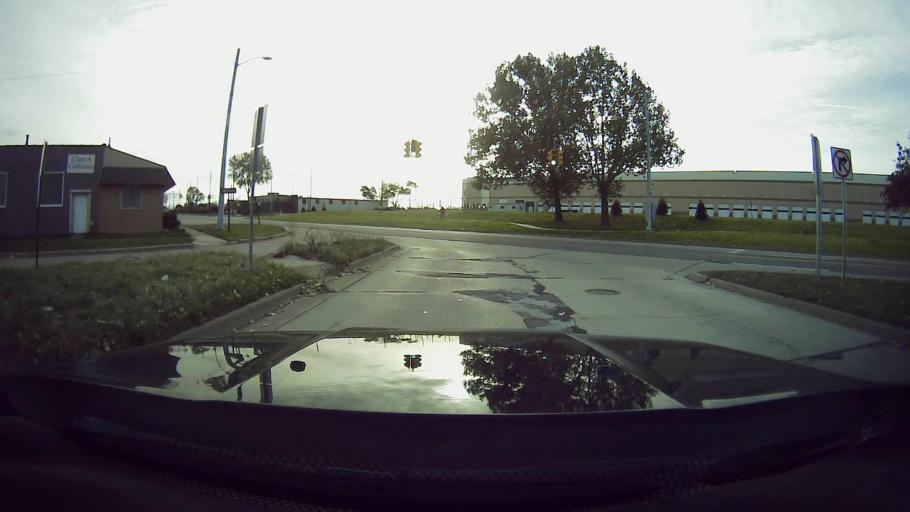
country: US
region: Michigan
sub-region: Oakland County
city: Madison Heights
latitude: 42.4765
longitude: -83.0914
